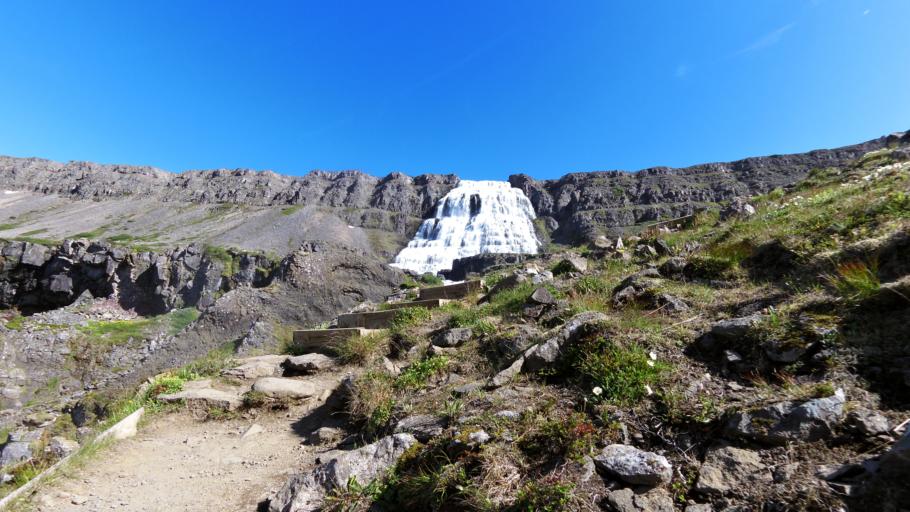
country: IS
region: Westfjords
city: Isafjoerdur
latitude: 65.7342
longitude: -23.2044
